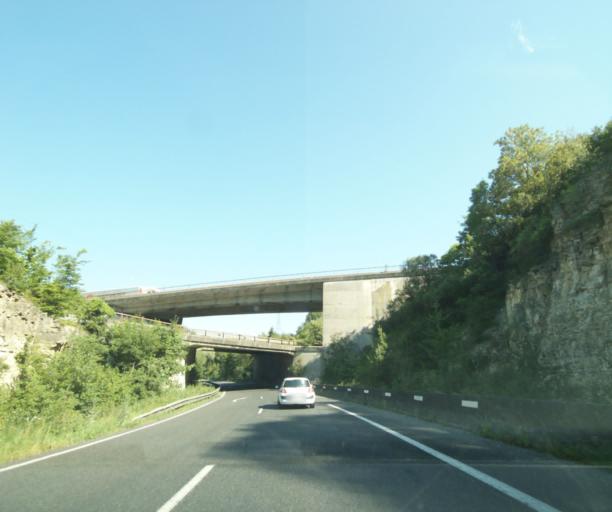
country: FR
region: Lorraine
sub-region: Departement de Meurthe-et-Moselle
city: Laxou
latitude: 48.6937
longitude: 6.1167
